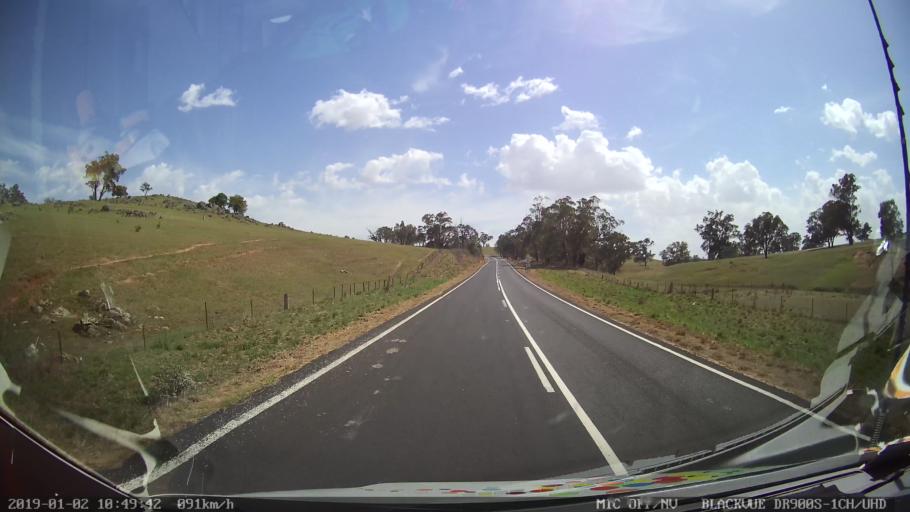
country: AU
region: New South Wales
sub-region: Cootamundra
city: Cootamundra
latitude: -34.7209
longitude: 148.2762
